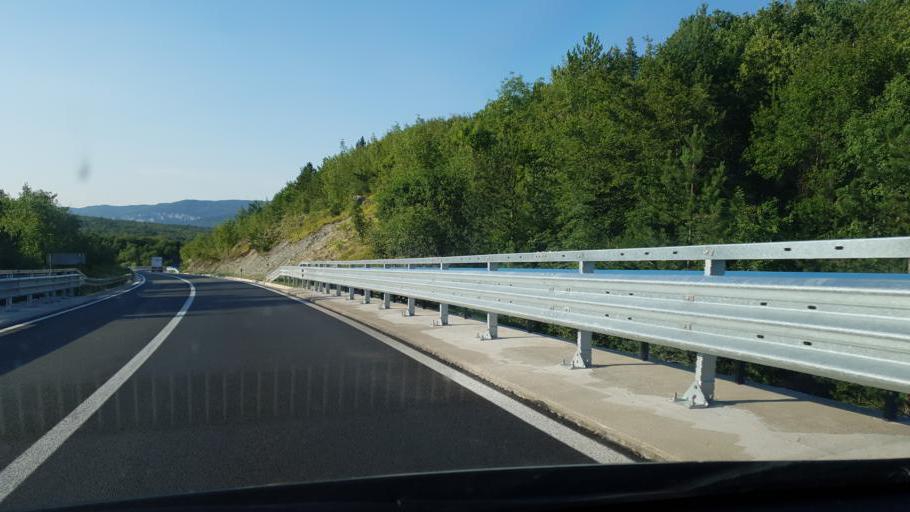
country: HR
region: Istarska
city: Buzet
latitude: 45.3388
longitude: 14.0789
